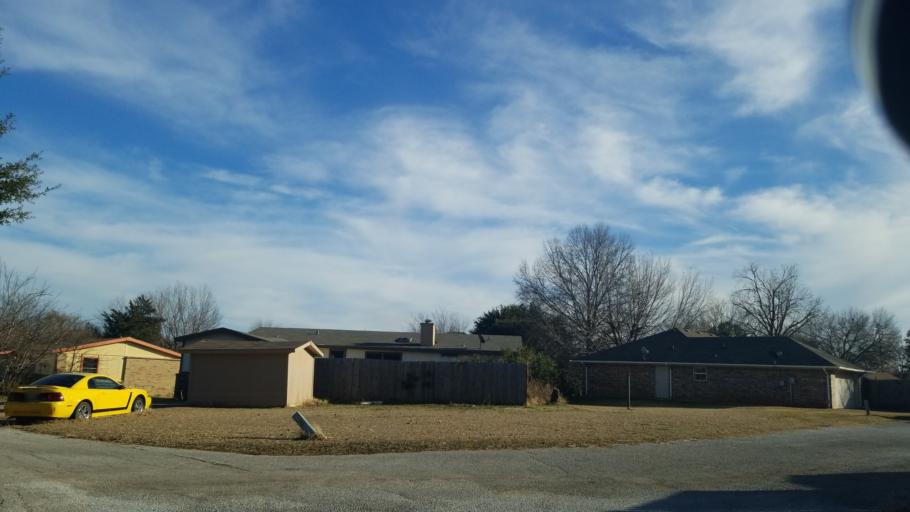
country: US
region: Texas
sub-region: Denton County
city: Corinth
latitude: 33.1379
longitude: -97.0621
